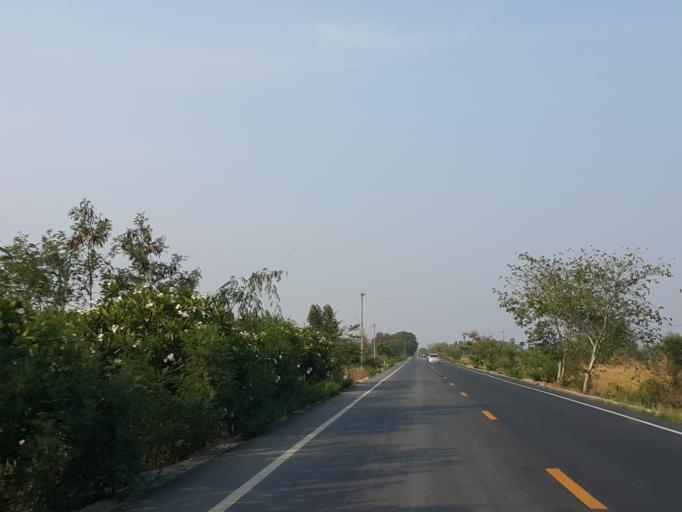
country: TH
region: Chai Nat
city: Sankhaburi
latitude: 14.9914
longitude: 100.1148
